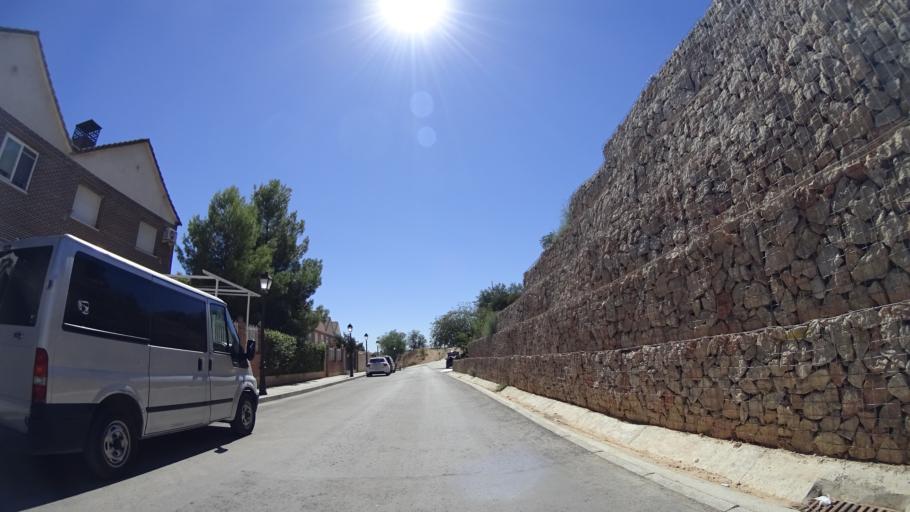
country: ES
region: Madrid
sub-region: Provincia de Madrid
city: Morata de Tajuna
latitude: 40.2318
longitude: -3.4414
